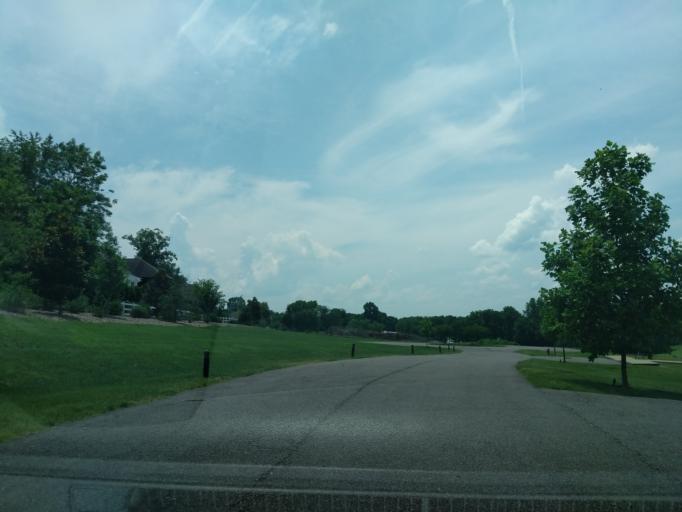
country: US
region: Tennessee
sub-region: Davidson County
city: Lakewood
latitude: 36.2330
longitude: -86.6350
